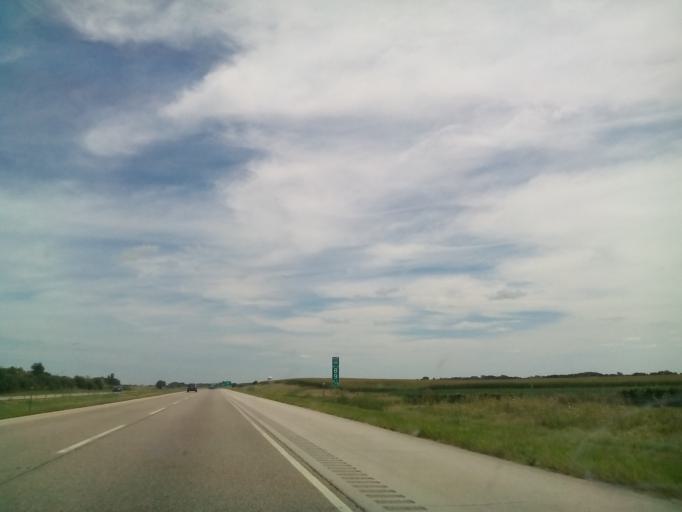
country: US
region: Illinois
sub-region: DeKalb County
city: Malta
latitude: 41.9001
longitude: -88.8068
